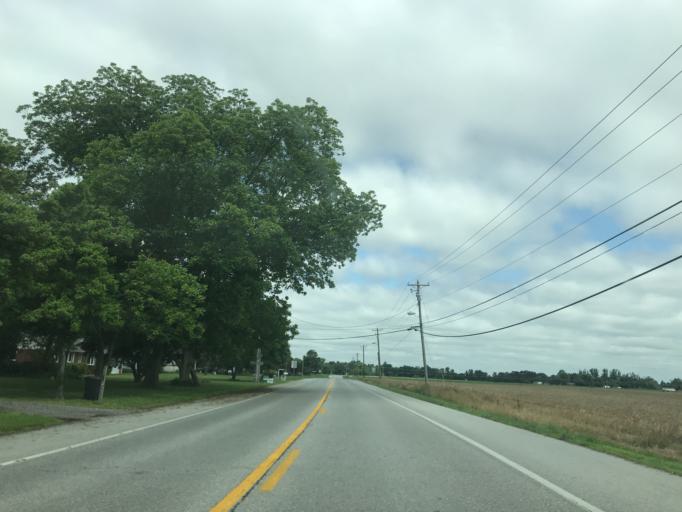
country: US
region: Maryland
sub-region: Caroline County
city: Ridgely
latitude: 38.9545
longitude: -75.8867
